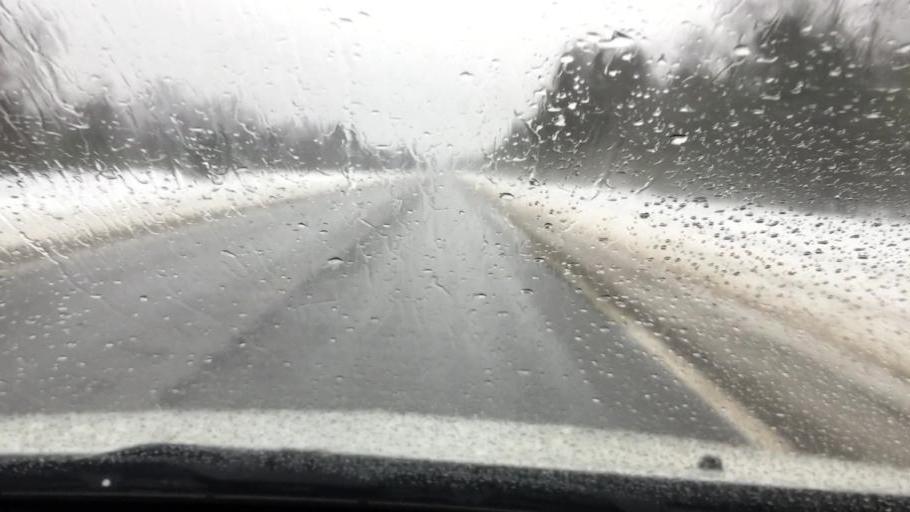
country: US
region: Michigan
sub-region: Charlevoix County
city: East Jordan
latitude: 45.0467
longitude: -85.0696
